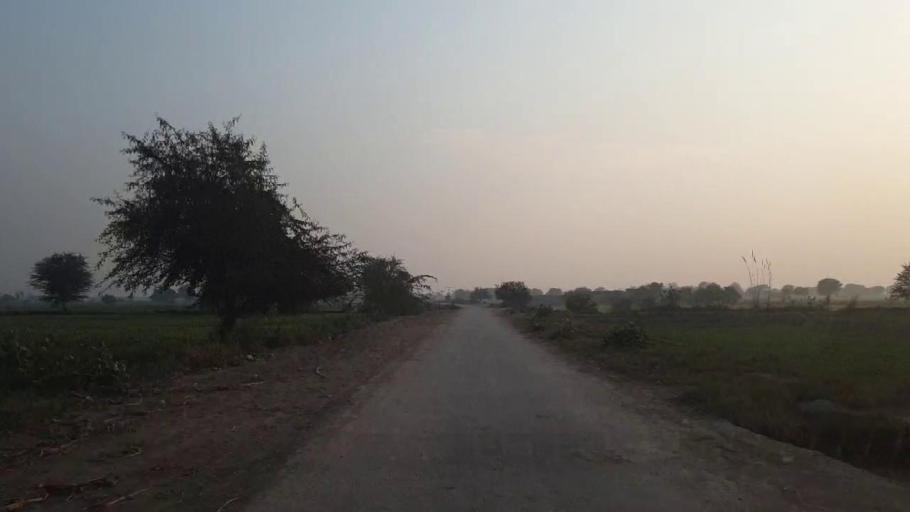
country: PK
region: Sindh
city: Bhit Shah
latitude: 25.7724
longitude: 68.4615
